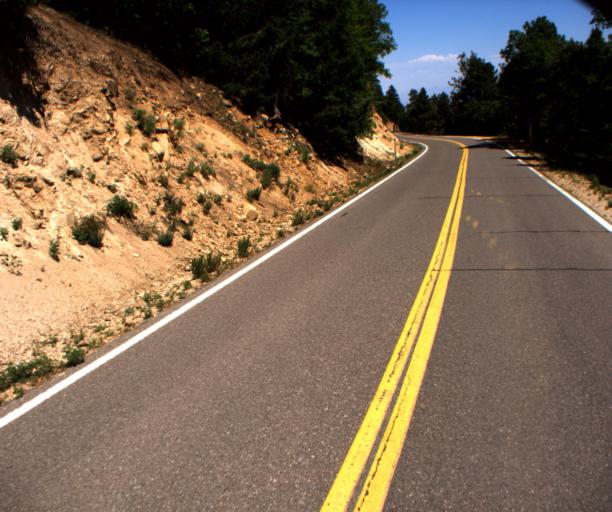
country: US
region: Arizona
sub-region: Graham County
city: Swift Trail Junction
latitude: 32.6252
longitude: -109.8340
